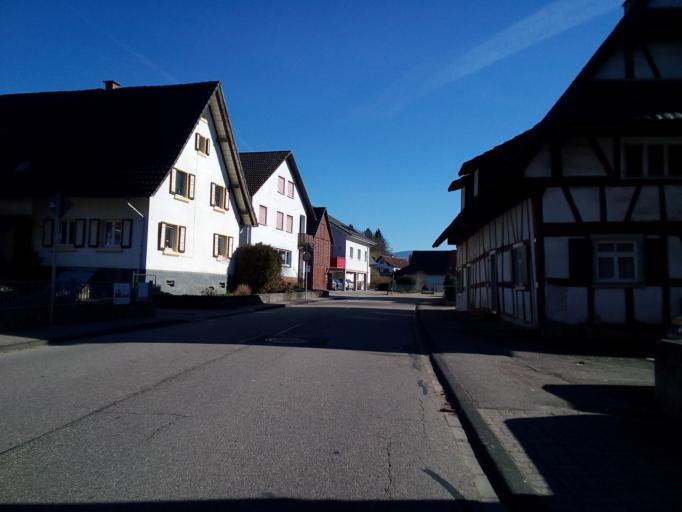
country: DE
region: Baden-Wuerttemberg
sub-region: Freiburg Region
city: Renchen
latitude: 48.6046
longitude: 8.0375
